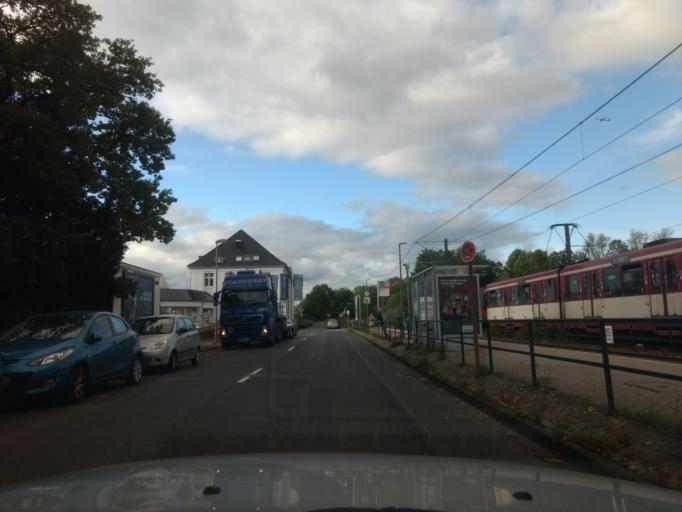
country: DE
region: North Rhine-Westphalia
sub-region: Regierungsbezirk Dusseldorf
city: Meerbusch
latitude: 51.2444
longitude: 6.7176
